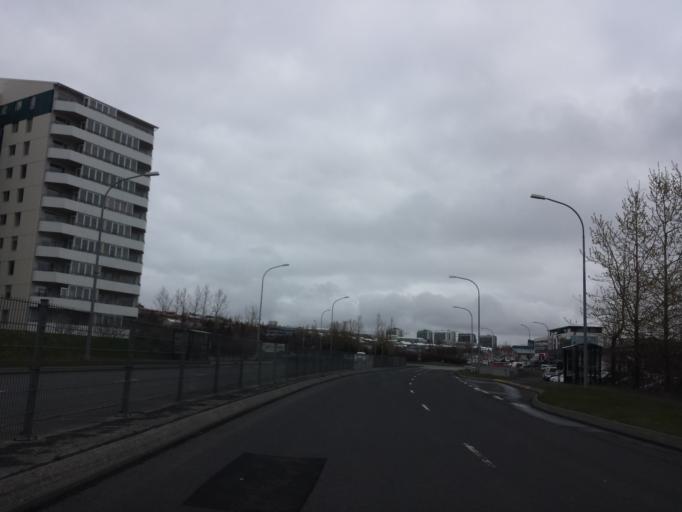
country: IS
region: Capital Region
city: Kopavogur
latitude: 64.1040
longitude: -21.8804
